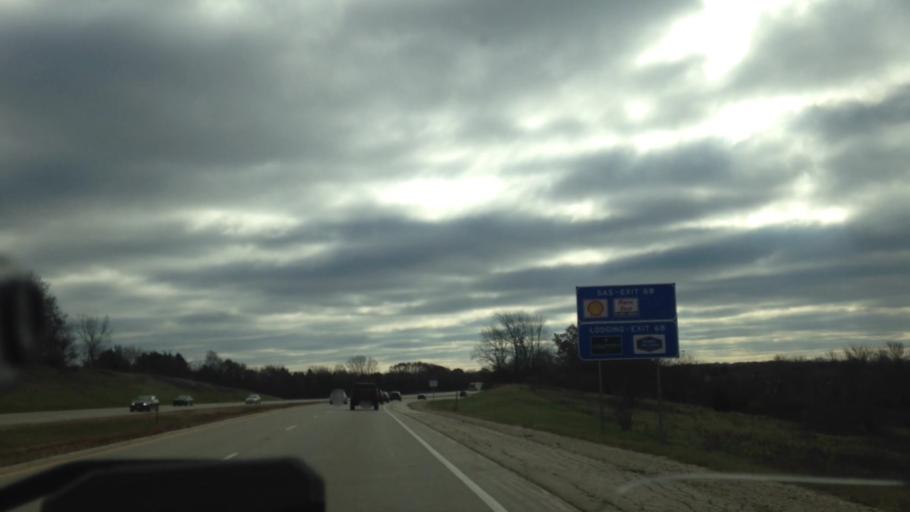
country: US
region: Wisconsin
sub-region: Washington County
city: West Bend
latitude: 43.4056
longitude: -88.1975
